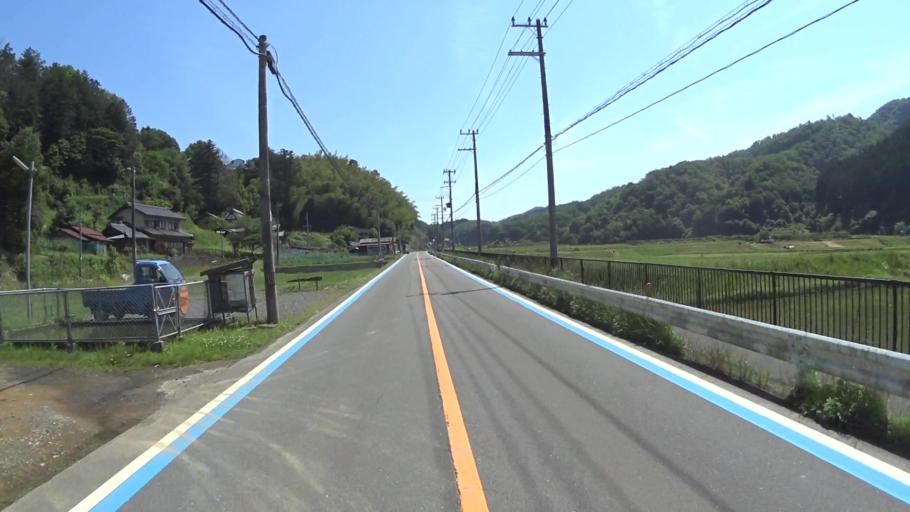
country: JP
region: Kyoto
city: Ayabe
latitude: 35.3374
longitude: 135.3506
